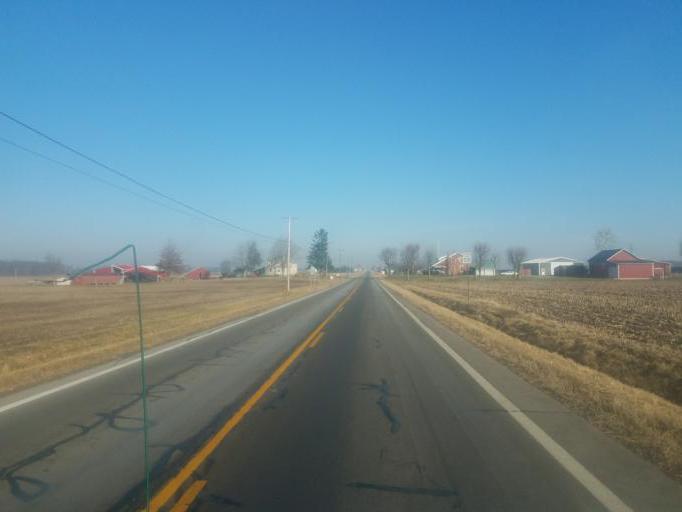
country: US
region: Ohio
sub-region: Crawford County
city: Bucyrus
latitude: 40.9580
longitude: -82.9401
